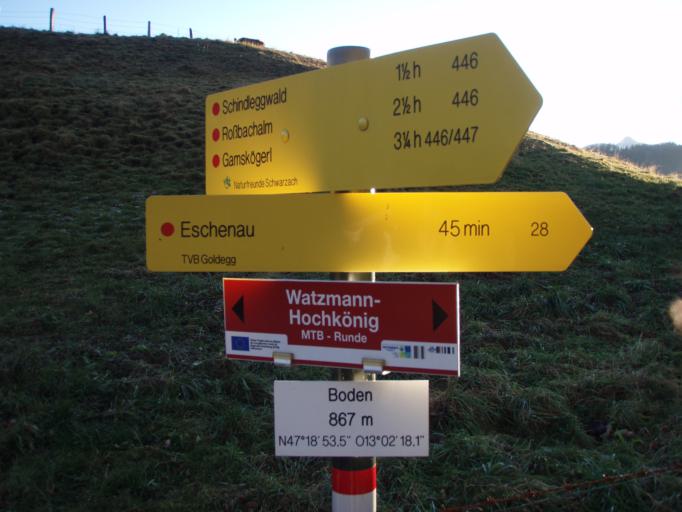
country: AT
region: Salzburg
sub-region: Politischer Bezirk Zell am See
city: Lend
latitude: 47.3144
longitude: 13.0377
